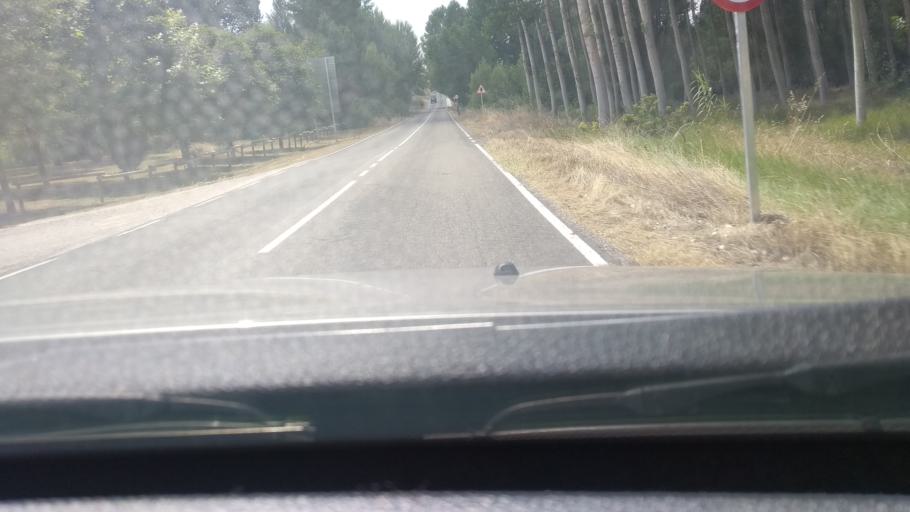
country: ES
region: Castille and Leon
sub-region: Provincia de Burgos
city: Villafruela
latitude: 41.9204
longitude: -3.9060
